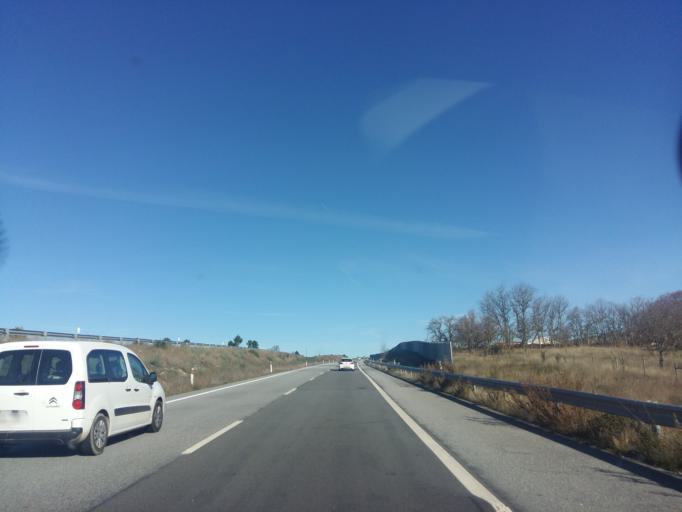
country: PT
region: Guarda
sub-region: Guarda
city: Sequeira
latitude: 40.5894
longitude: -7.1453
